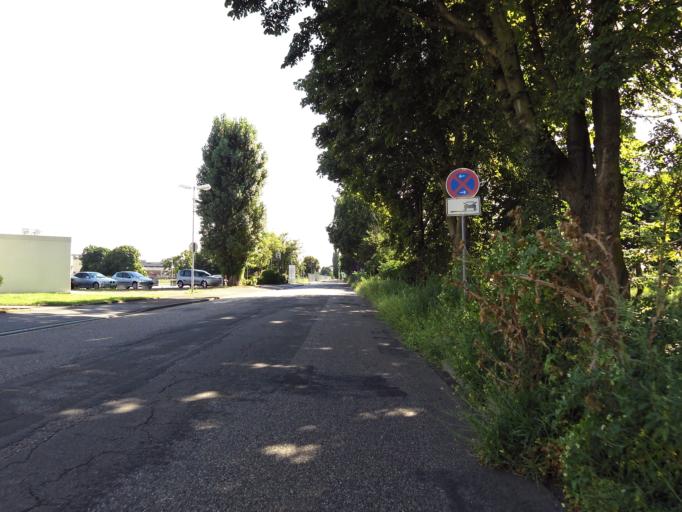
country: DE
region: Rheinland-Pfalz
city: Worms
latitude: 49.6555
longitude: 8.3627
